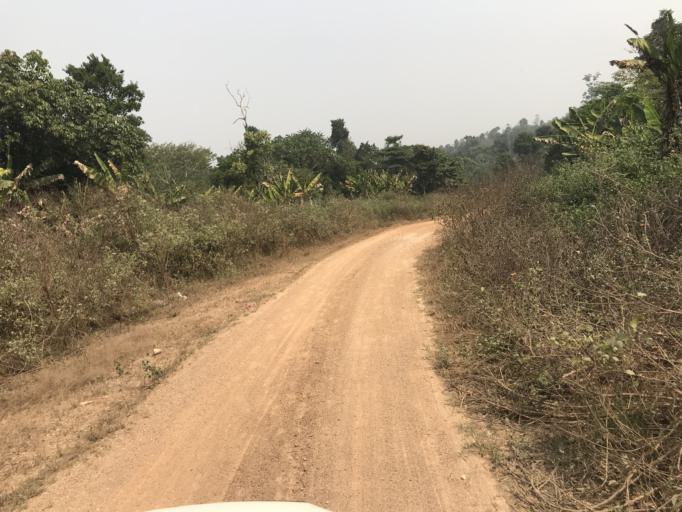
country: NG
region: Osun
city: Ifetedo
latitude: 7.0443
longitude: 4.4625
